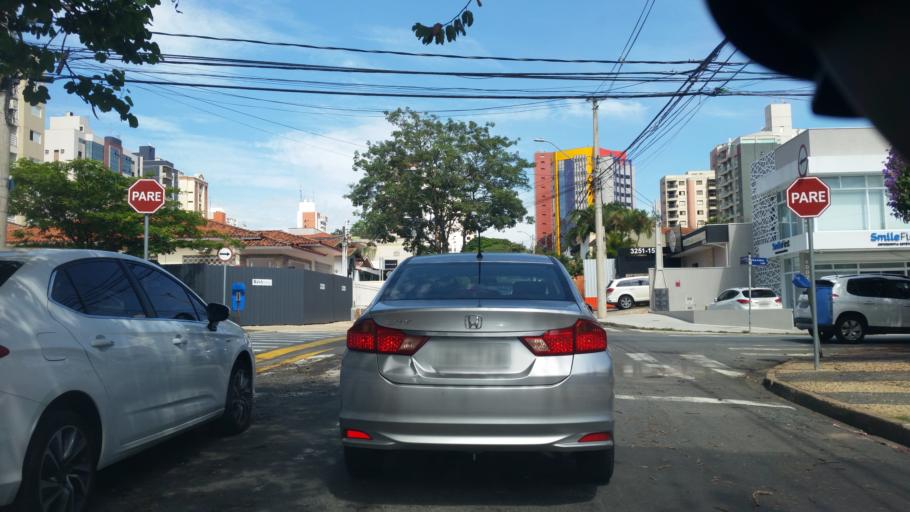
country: BR
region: Sao Paulo
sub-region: Campinas
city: Campinas
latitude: -22.8921
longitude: -47.0499
